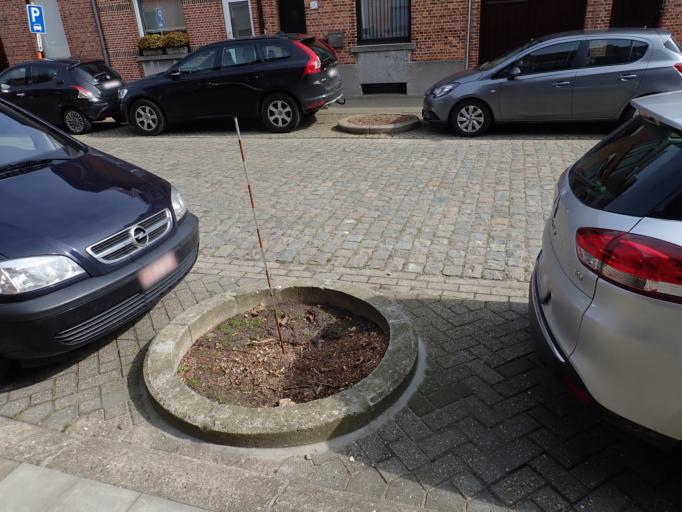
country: BE
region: Flanders
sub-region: Provincie Antwerpen
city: Zwijndrecht
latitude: 51.2059
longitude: 4.3466
